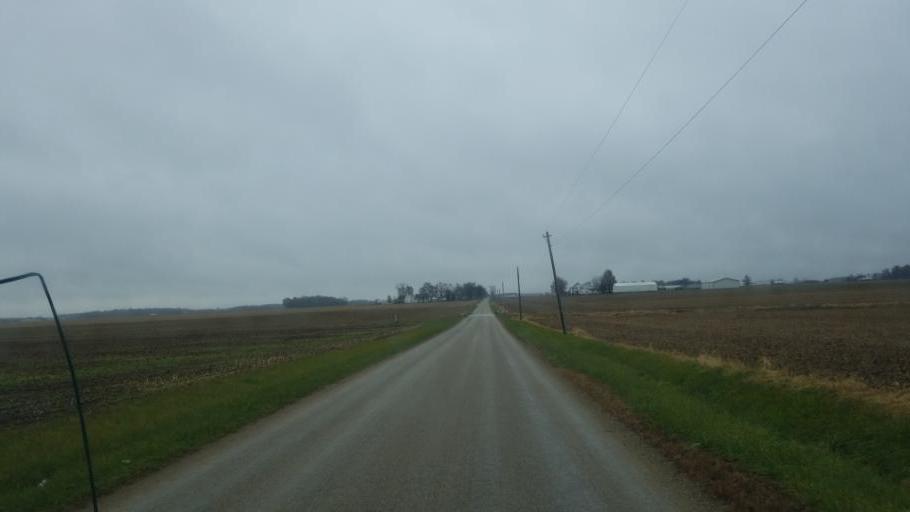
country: US
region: Indiana
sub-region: Adams County
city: Berne
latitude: 40.6764
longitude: -84.9172
